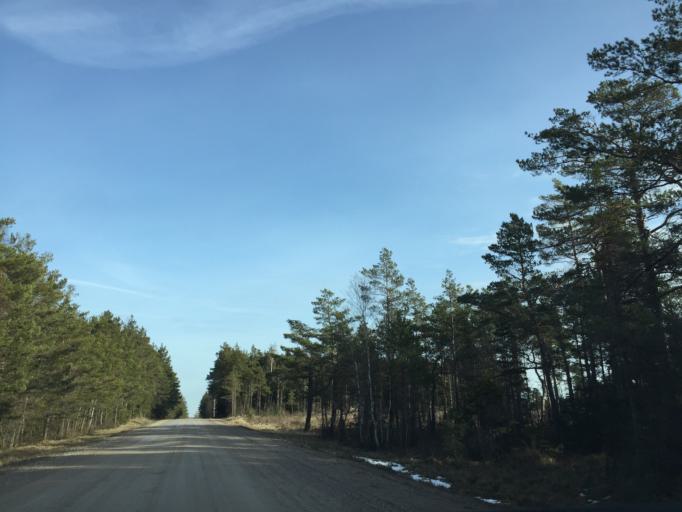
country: EE
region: Saare
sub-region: Kuressaare linn
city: Kuressaare
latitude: 58.3130
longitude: 21.9830
